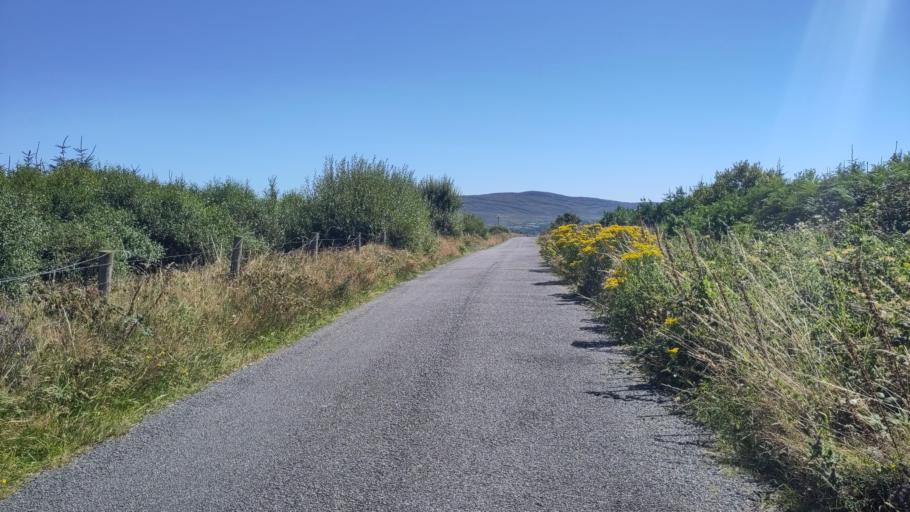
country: IE
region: Munster
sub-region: Ciarrai
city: Kenmare
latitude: 51.6669
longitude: -9.9114
